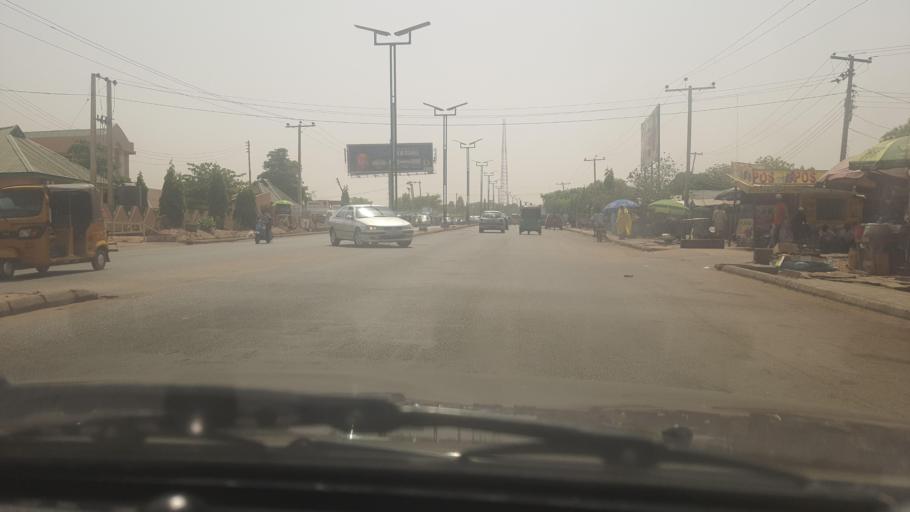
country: NG
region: Gombe
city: Gombe
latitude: 10.2863
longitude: 11.1388
